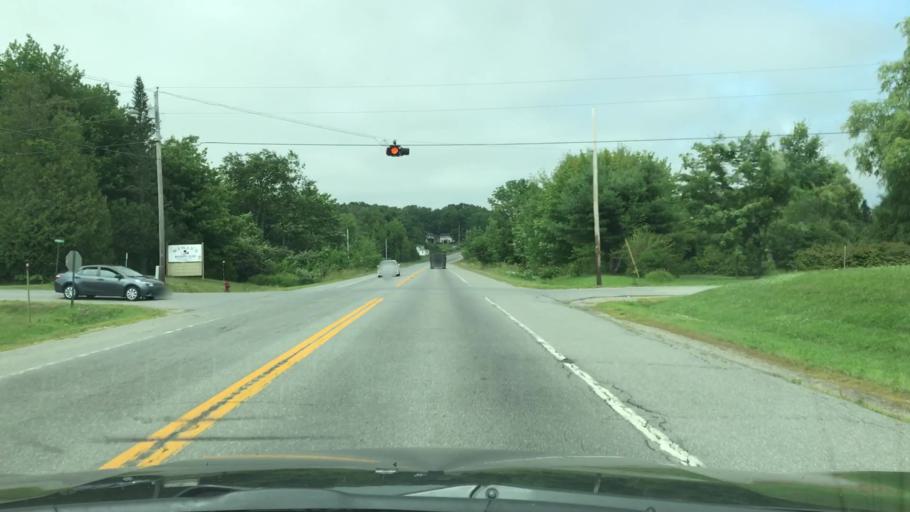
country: US
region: Maine
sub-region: Waldo County
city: Stockton Springs
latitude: 44.4872
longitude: -68.8633
